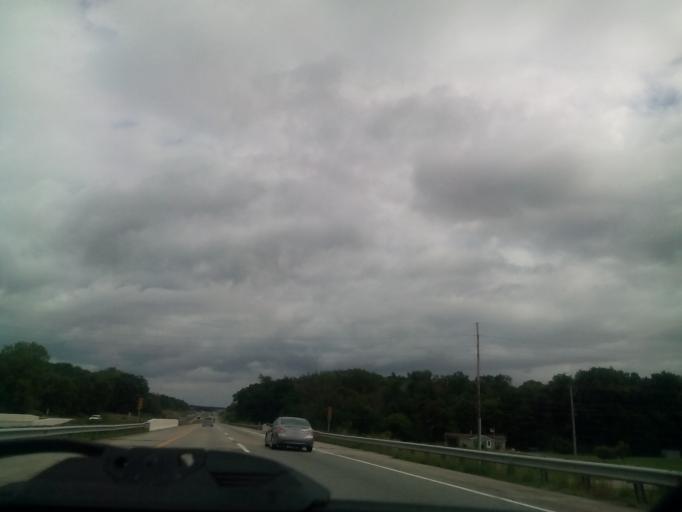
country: US
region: Indiana
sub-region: Steuben County
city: Fremont
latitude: 41.7110
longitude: -84.9415
